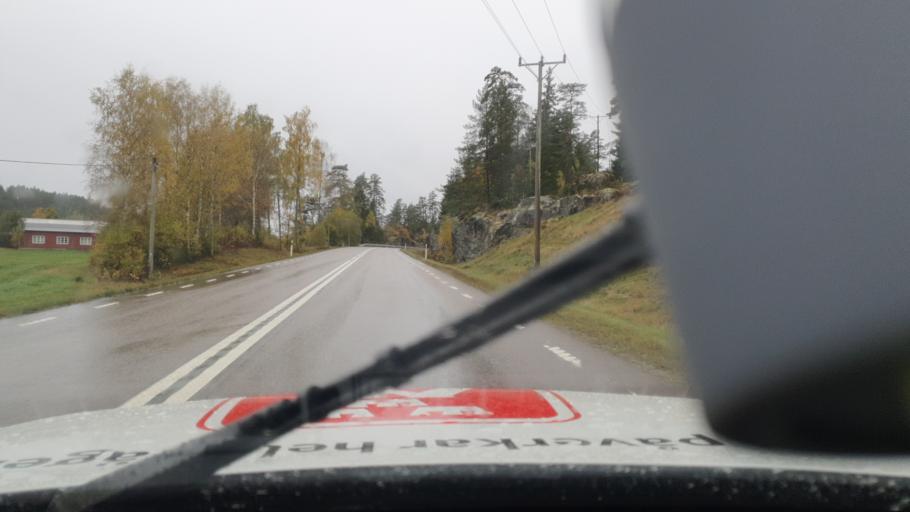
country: SE
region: Vaestra Goetaland
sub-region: Dals-Ed Kommun
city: Ed
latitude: 58.9352
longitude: 12.0677
